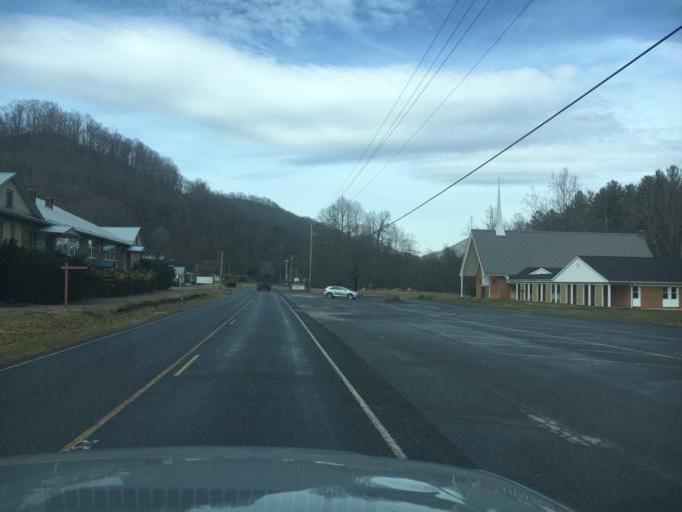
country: US
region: North Carolina
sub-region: Haywood County
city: Canton
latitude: 35.4186
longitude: -82.8119
